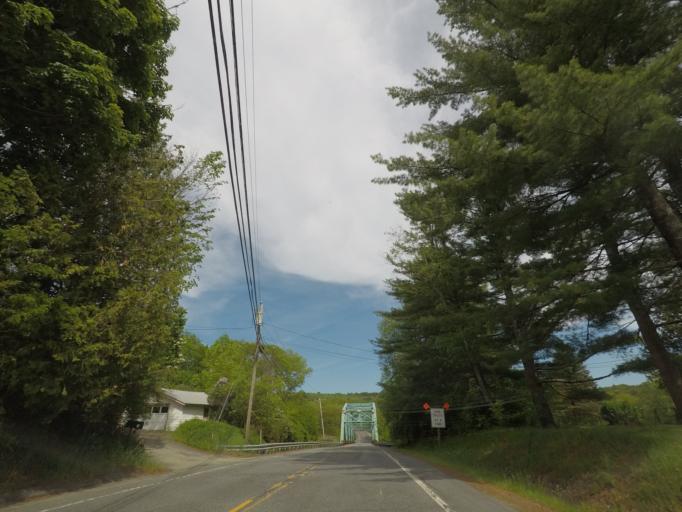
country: US
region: Maine
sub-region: Sagadahoc County
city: Richmond
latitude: 44.0842
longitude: -69.7498
